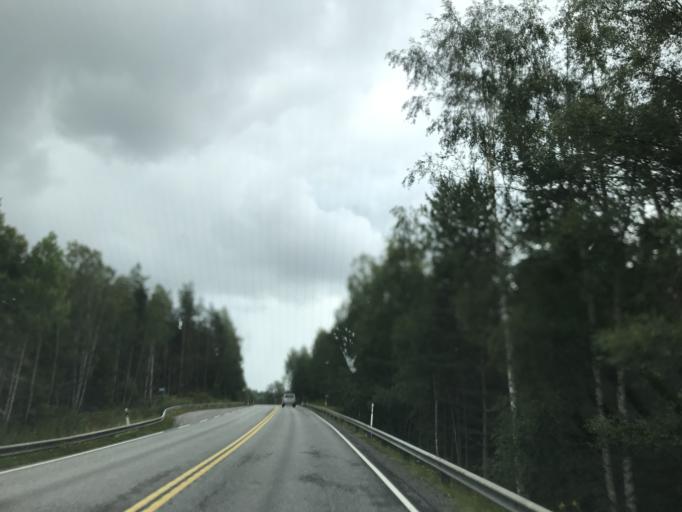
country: FI
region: Varsinais-Suomi
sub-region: Salo
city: Pernioe
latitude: 60.0814
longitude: 23.2397
